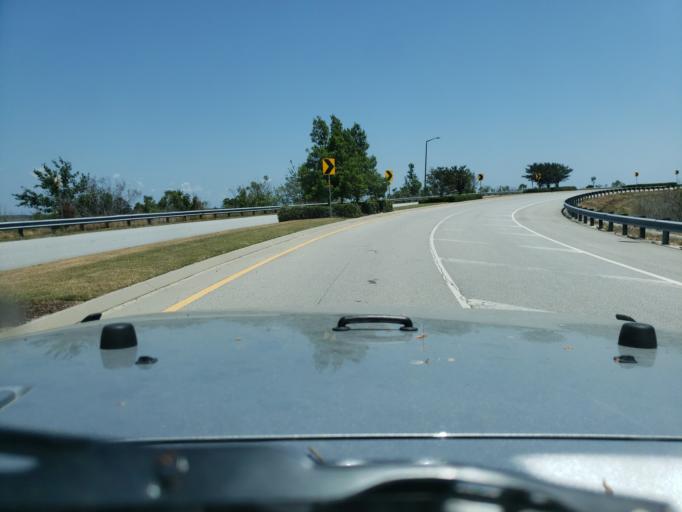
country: US
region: Georgia
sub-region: Chatham County
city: Savannah
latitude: 32.0980
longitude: -81.0949
